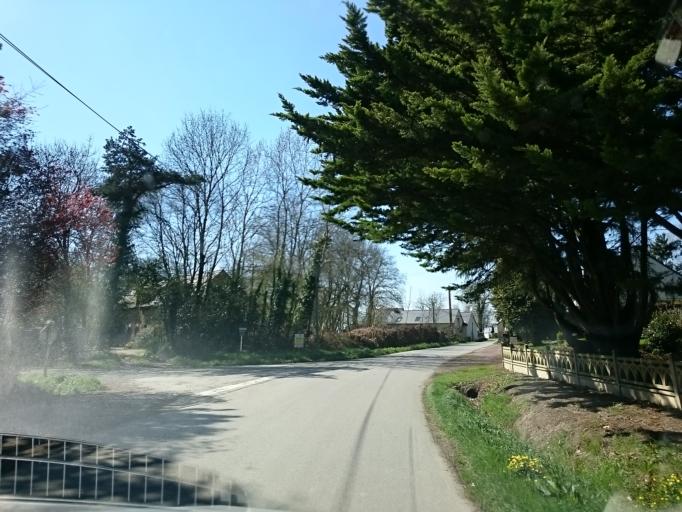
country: FR
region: Brittany
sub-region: Departement d'Ille-et-Vilaine
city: Crevin
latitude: 47.9639
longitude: -1.6801
